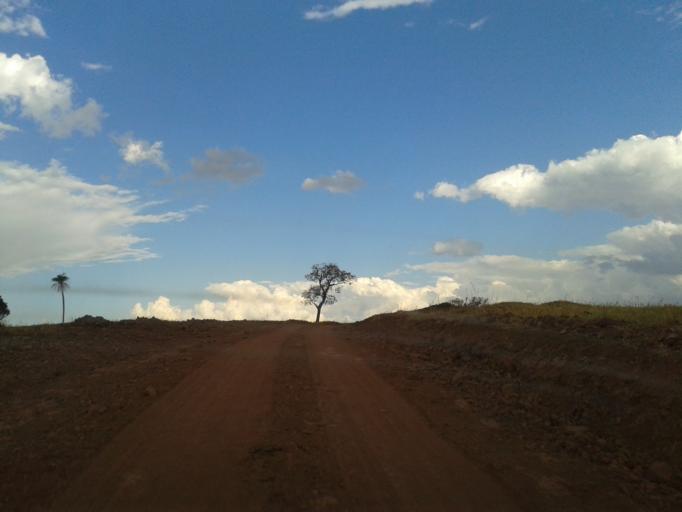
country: BR
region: Minas Gerais
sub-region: Santa Vitoria
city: Santa Vitoria
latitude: -19.1834
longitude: -49.9432
